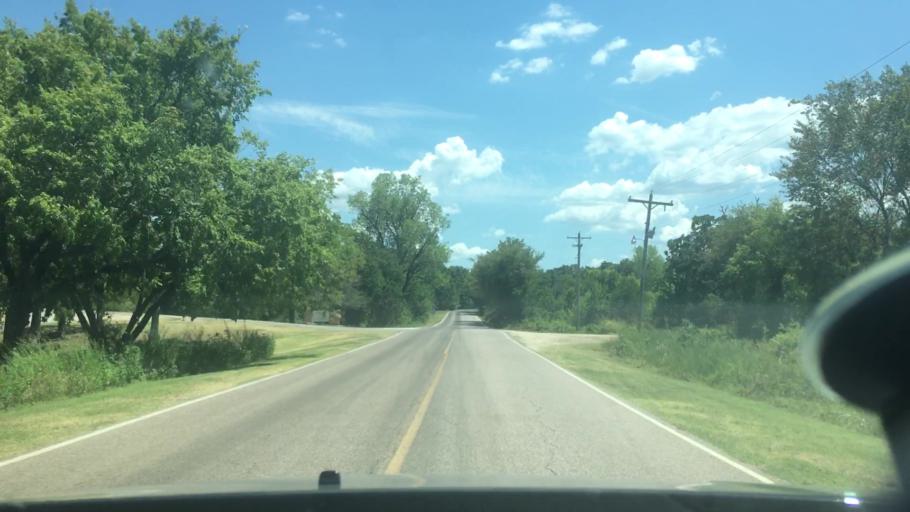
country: US
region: Oklahoma
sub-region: Marshall County
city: Kingston
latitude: 33.9885
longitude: -96.6379
